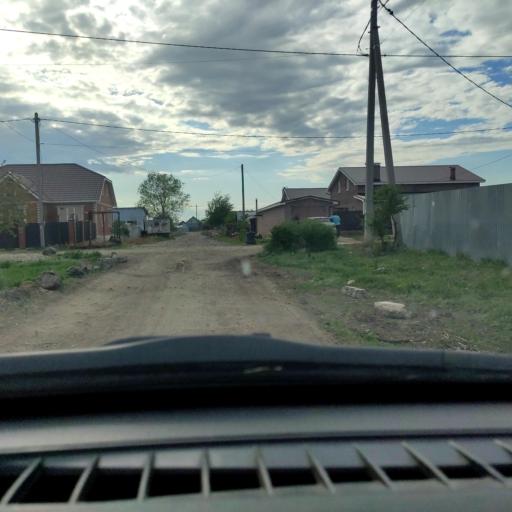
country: RU
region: Samara
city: Tol'yatti
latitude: 53.5749
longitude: 49.4125
